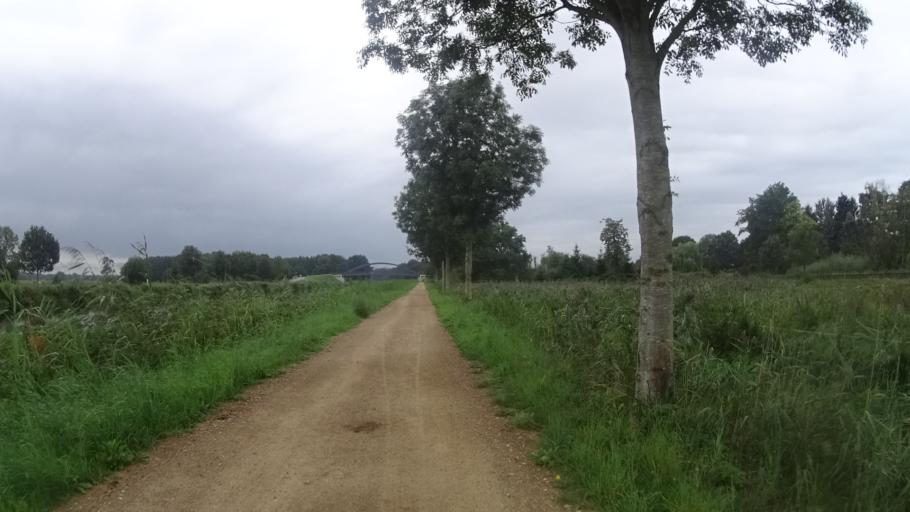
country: DE
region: Schleswig-Holstein
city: Dalldorf
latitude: 53.4369
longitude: 10.6156
